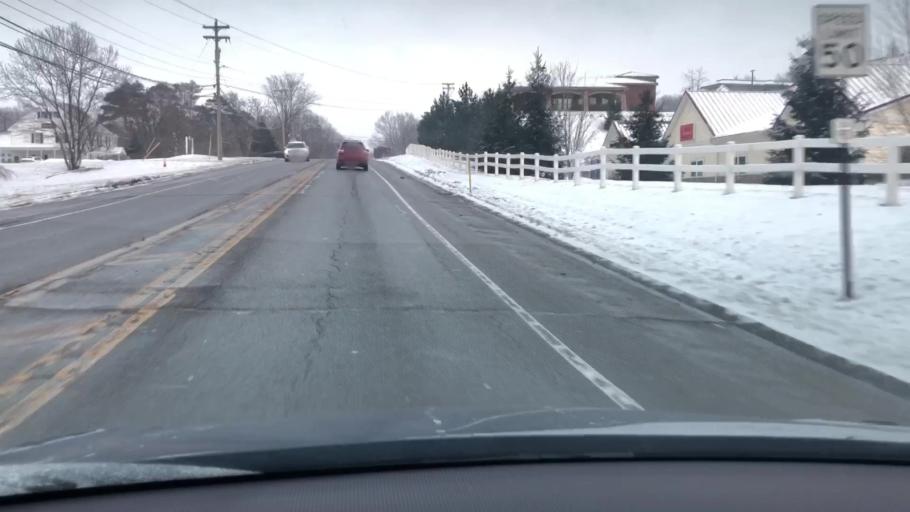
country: US
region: Pennsylvania
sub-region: Butler County
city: Seven Fields
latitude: 40.6964
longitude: -80.0374
